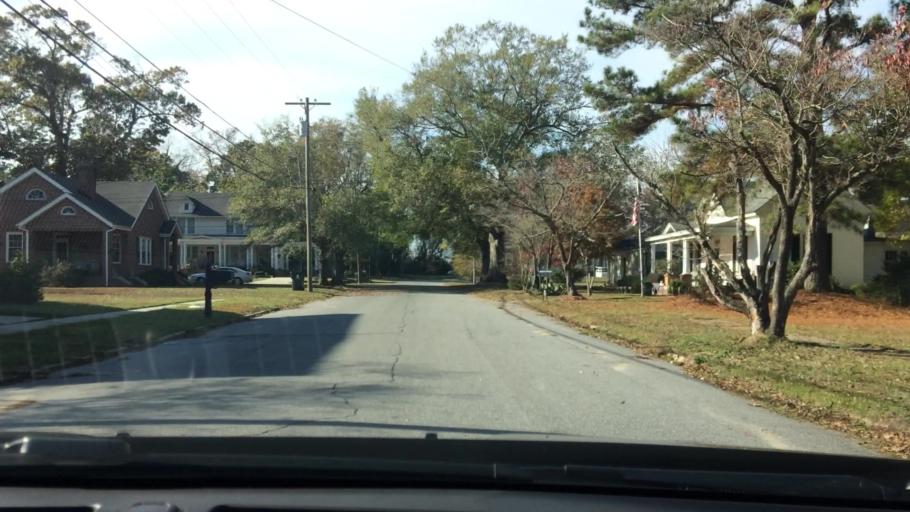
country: US
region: North Carolina
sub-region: Greene County
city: Snow Hill
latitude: 35.4538
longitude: -77.6736
